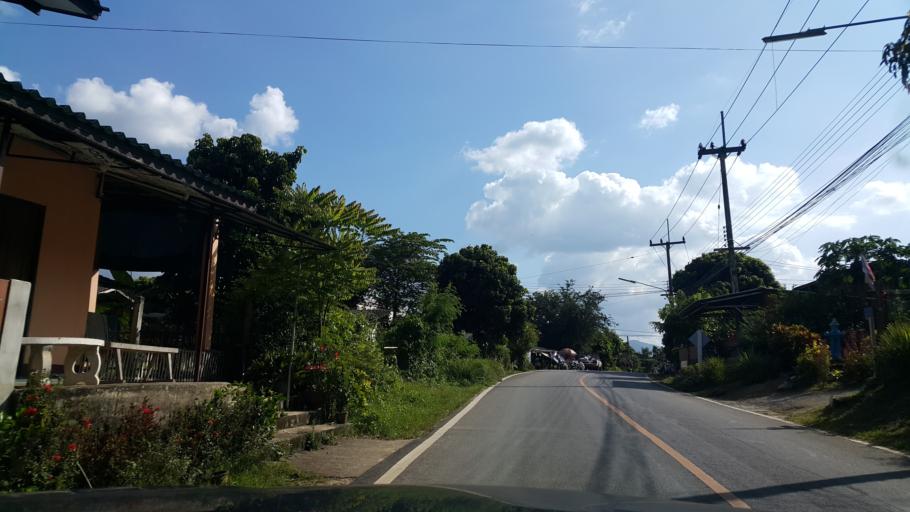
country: TH
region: Lamphun
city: Mae Tha
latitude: 18.5642
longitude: 99.2581
